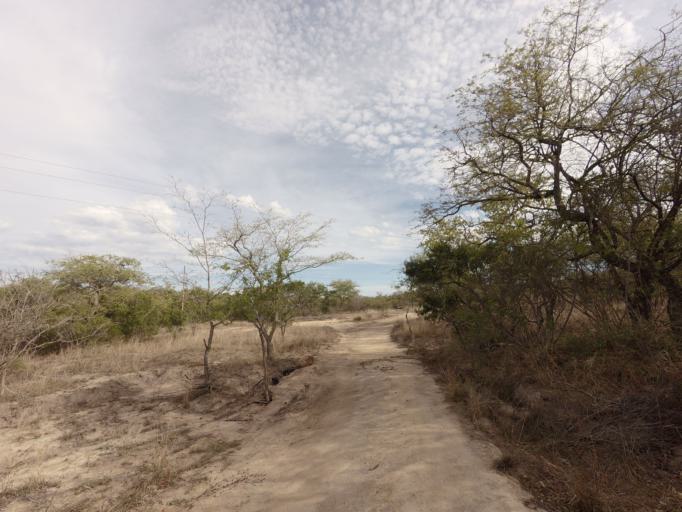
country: ZA
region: Limpopo
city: Thulamahashi
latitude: -24.5241
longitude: 31.1224
